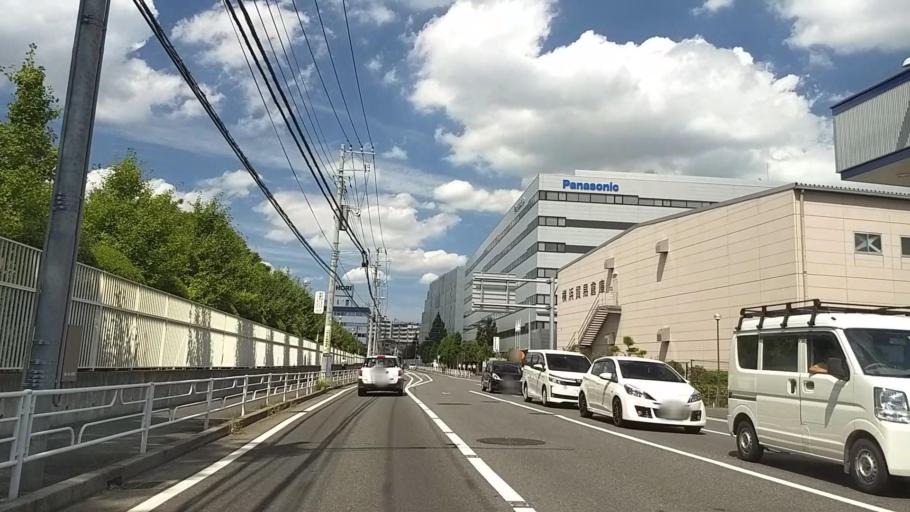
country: JP
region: Kanagawa
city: Yokohama
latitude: 35.5153
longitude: 139.5637
